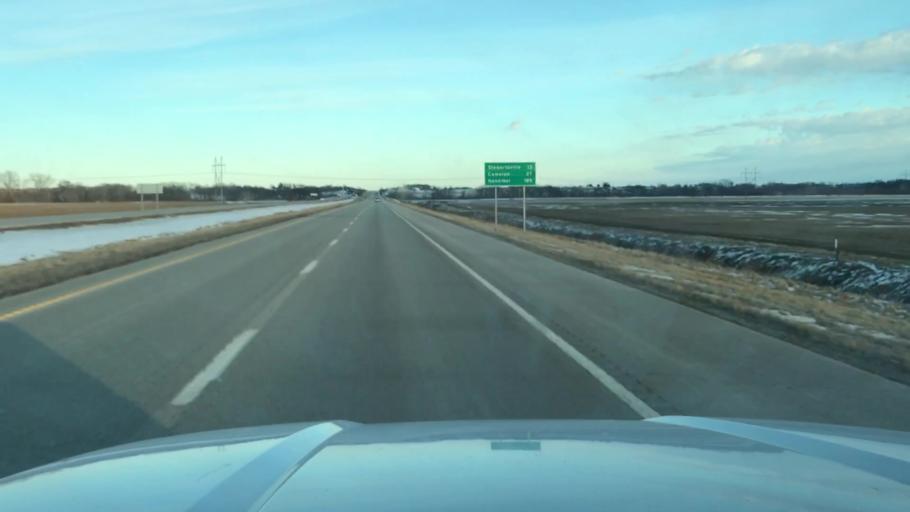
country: US
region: Missouri
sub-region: Buchanan County
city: Saint Joseph
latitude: 39.7479
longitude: -94.7381
